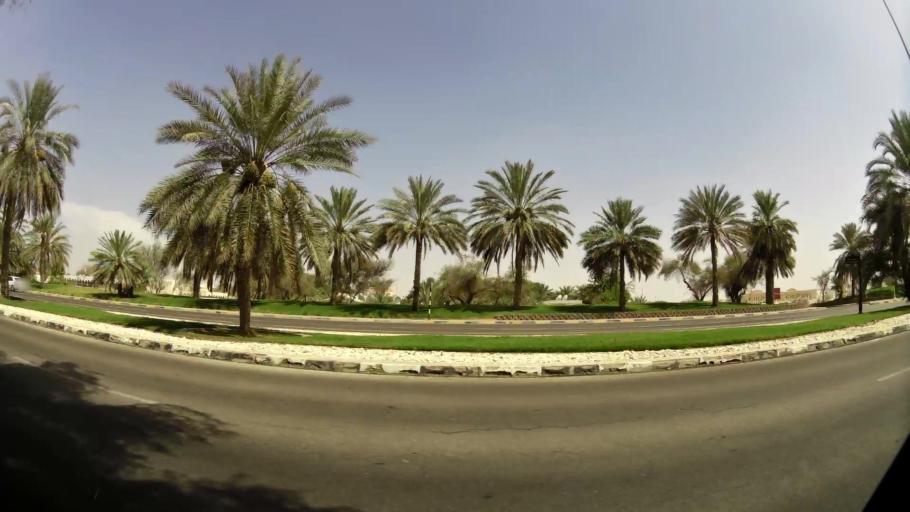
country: AE
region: Abu Dhabi
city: Al Ain
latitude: 24.2254
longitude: 55.7066
